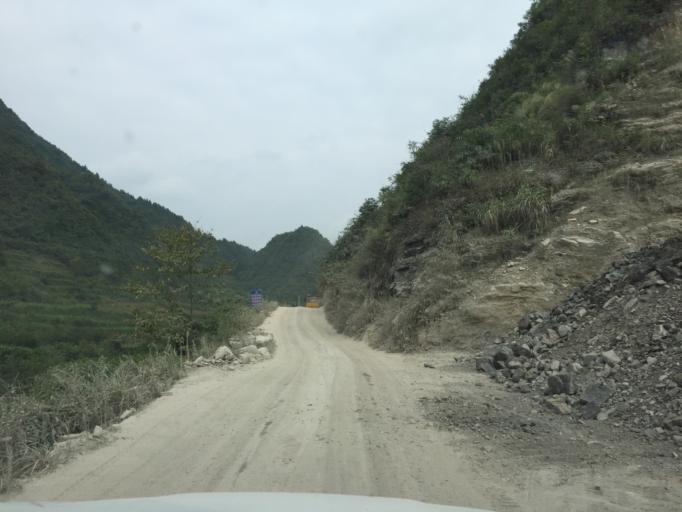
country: CN
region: Guizhou Sheng
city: Longquan
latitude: 28.1956
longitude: 108.0457
